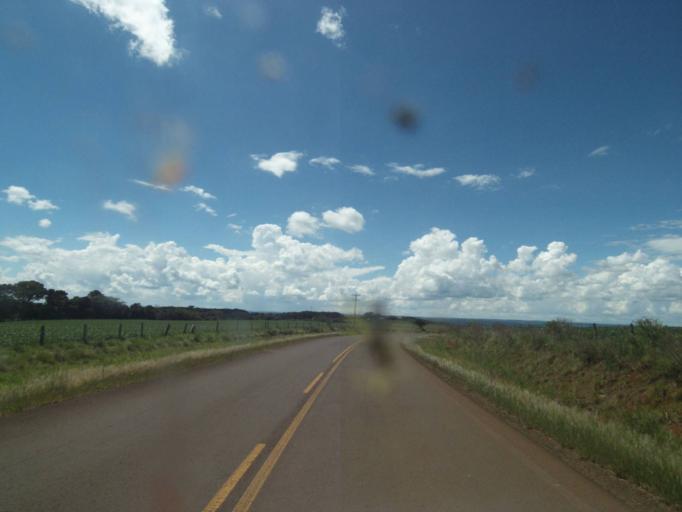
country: BR
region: Parana
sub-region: Pinhao
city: Pinhao
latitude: -25.8002
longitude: -52.0747
